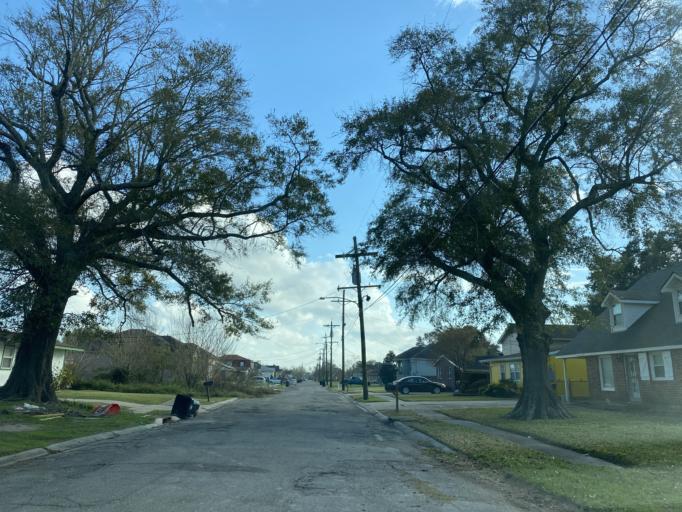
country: US
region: Louisiana
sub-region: Saint Bernard Parish
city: Arabi
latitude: 30.0292
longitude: -90.0379
